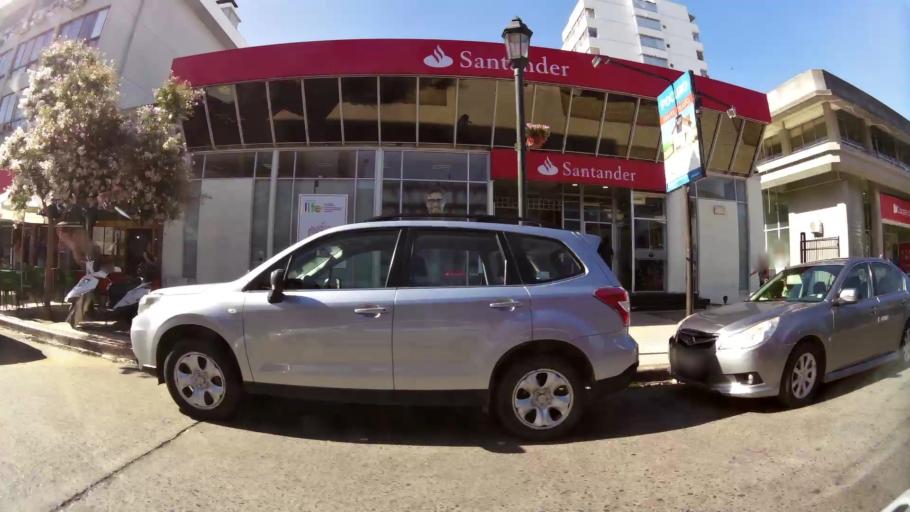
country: CL
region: Maule
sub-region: Provincia de Talca
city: Talca
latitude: -35.4272
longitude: -71.6646
